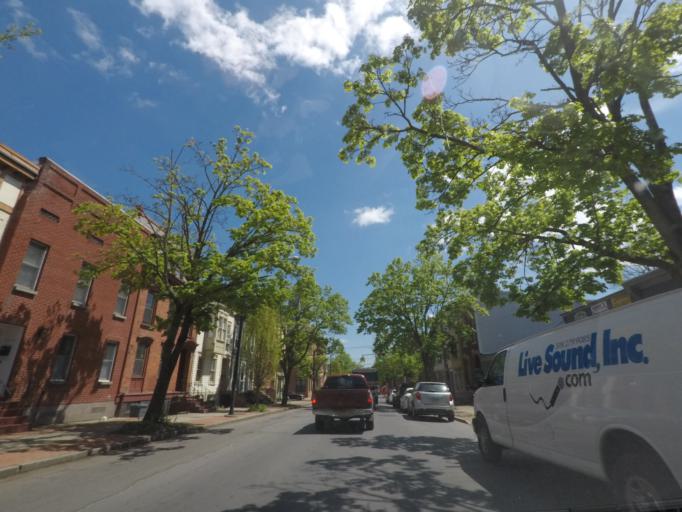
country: US
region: New York
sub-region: Albany County
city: Albany
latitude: 42.6516
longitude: -73.7661
